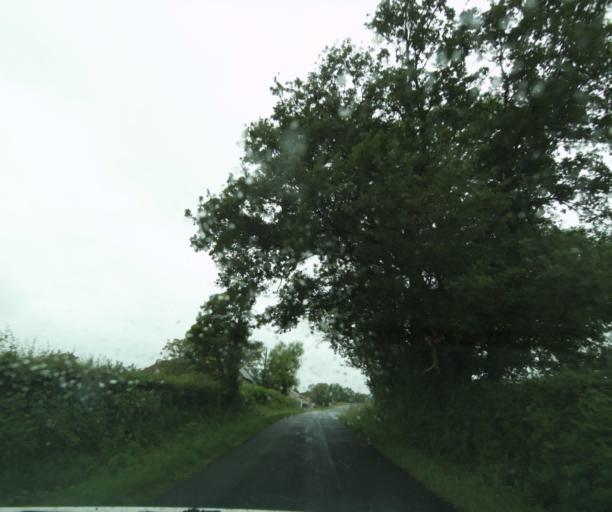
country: FR
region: Bourgogne
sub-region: Departement de Saone-et-Loire
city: Palinges
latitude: 46.5442
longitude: 4.1776
